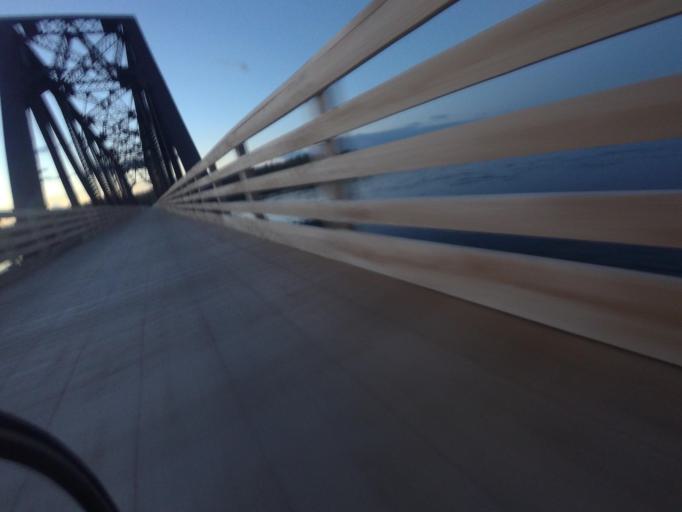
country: CA
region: Ontario
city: Arnprior
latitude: 45.4660
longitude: -76.2860
